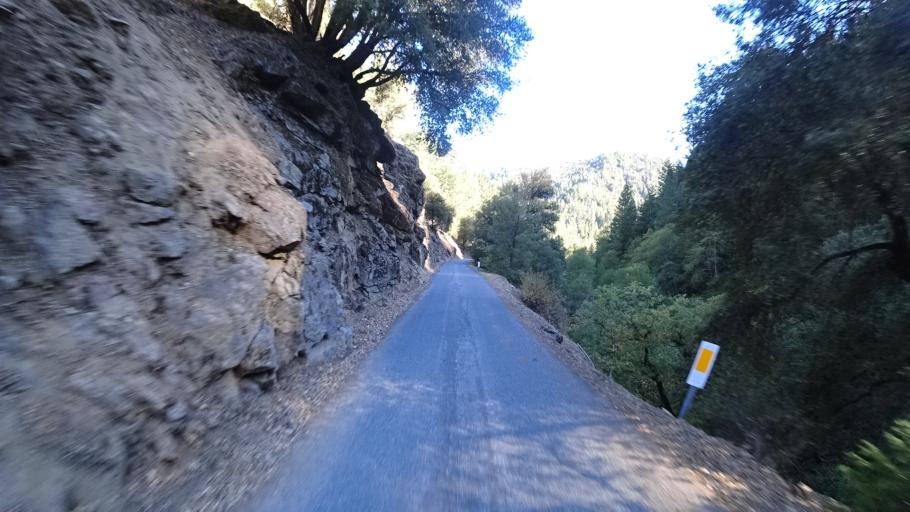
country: US
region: California
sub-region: Siskiyou County
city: Happy Camp
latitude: 41.3192
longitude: -123.1738
